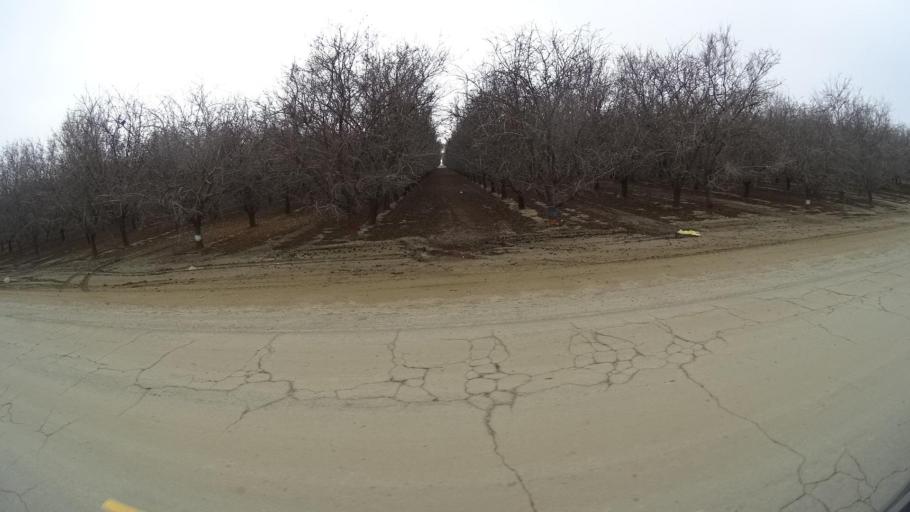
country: US
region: California
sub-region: Kern County
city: Maricopa
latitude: 35.0937
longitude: -119.2418
